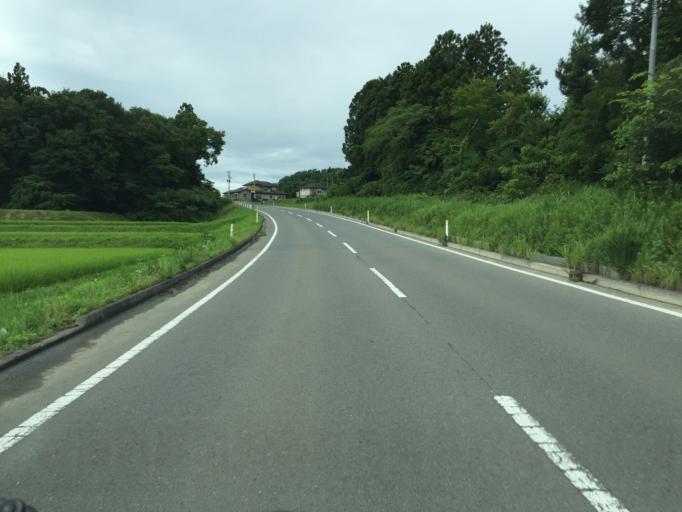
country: JP
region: Miyagi
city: Marumori
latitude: 37.7787
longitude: 140.9503
